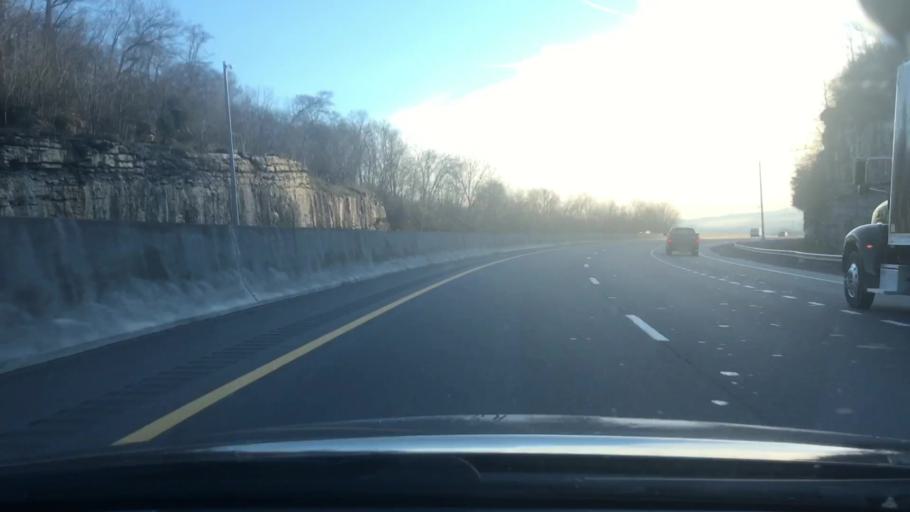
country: US
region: Tennessee
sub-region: Davidson County
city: Nashville
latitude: 36.2294
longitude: -86.8410
